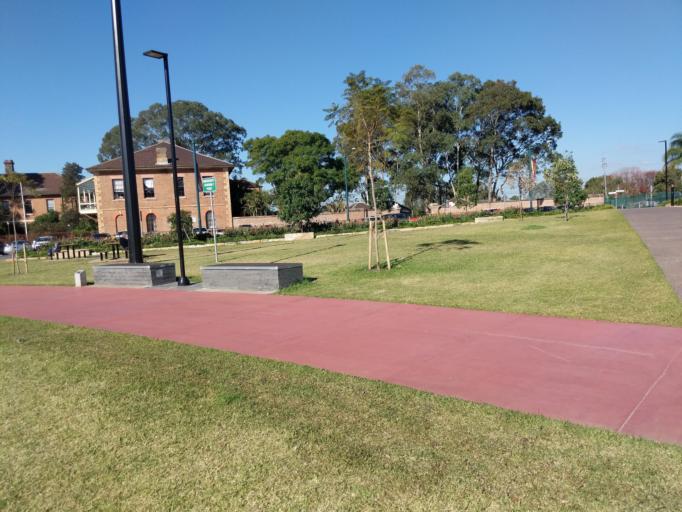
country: AU
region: New South Wales
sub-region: Fairfield
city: Liverpool
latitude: -33.9221
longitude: 150.9284
